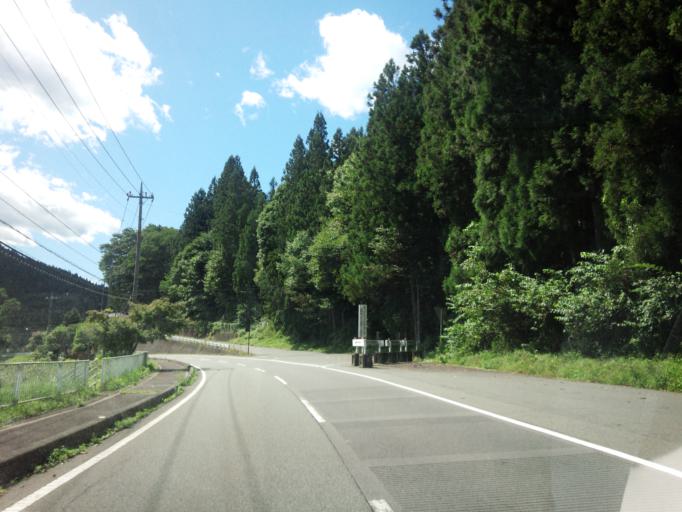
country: JP
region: Gunma
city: Nakanojomachi
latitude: 36.6511
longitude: 138.7982
